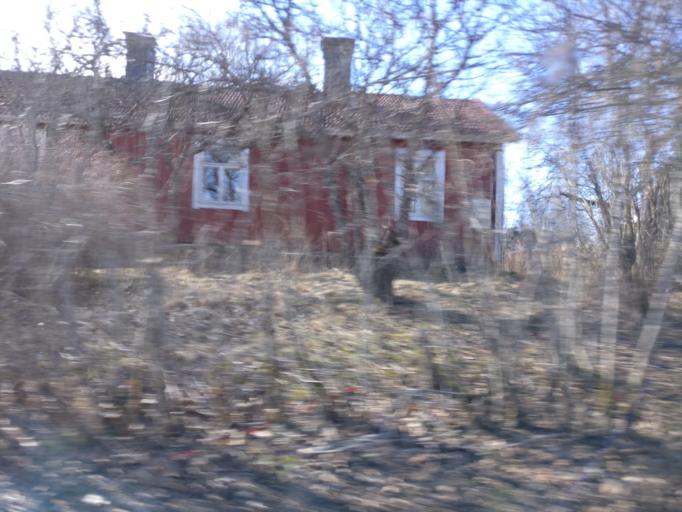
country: FI
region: Uusimaa
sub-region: Helsinki
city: Karjalohja
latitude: 60.2790
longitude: 23.6585
